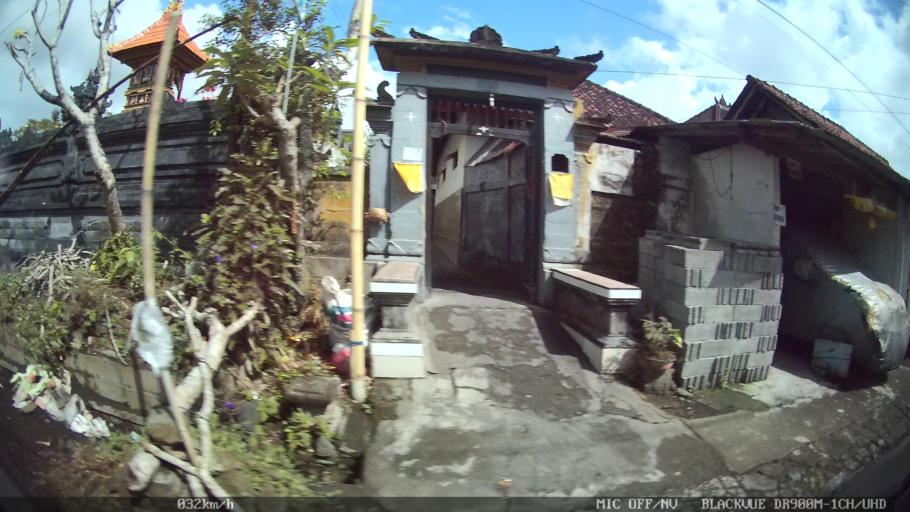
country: ID
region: Bali
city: Banjar Karangsuling
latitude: -8.5958
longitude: 115.1977
